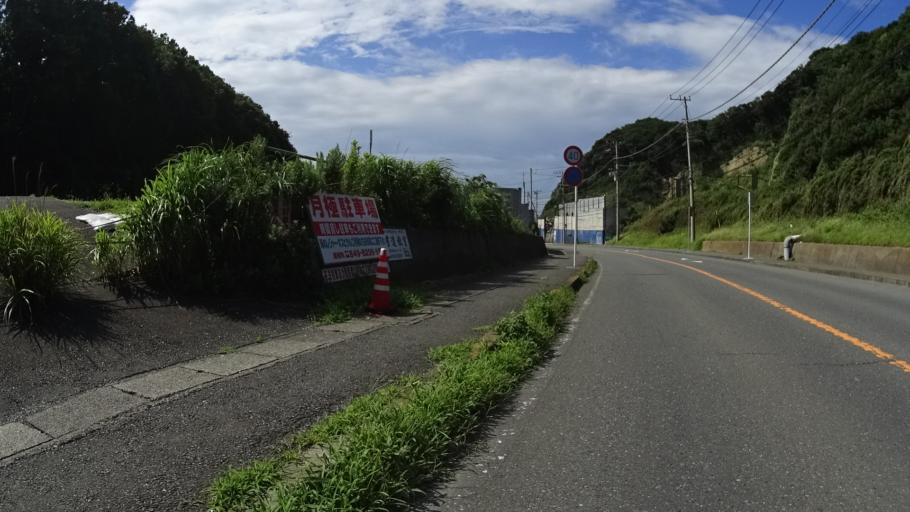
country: JP
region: Kanagawa
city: Yokosuka
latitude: 35.2131
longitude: 139.7110
